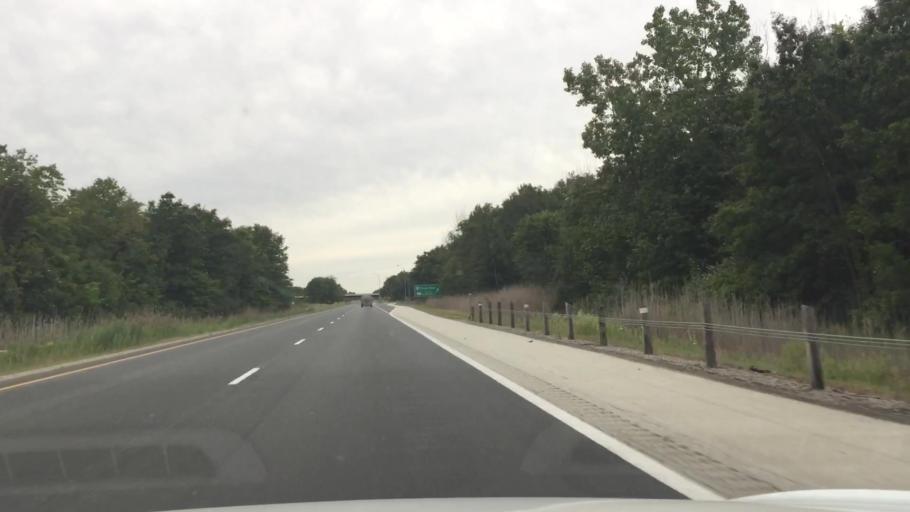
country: CA
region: Ontario
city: Camlachie
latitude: 42.9917
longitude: -81.9943
